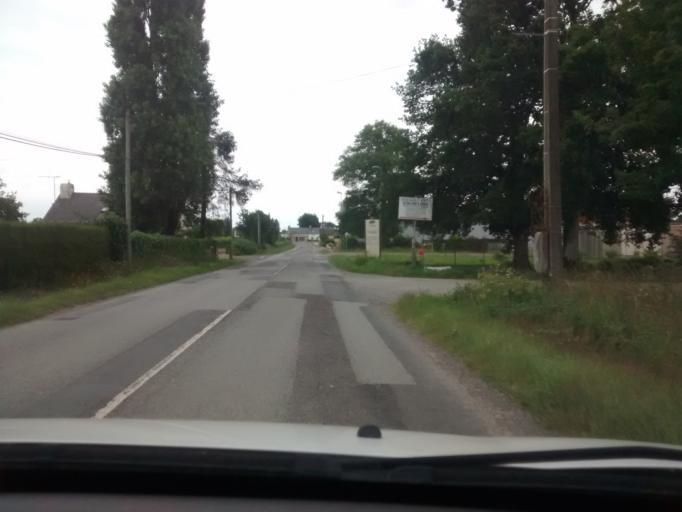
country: FR
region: Brittany
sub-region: Departement d'Ille-et-Vilaine
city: La Bouexiere
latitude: 48.1730
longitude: -1.4361
